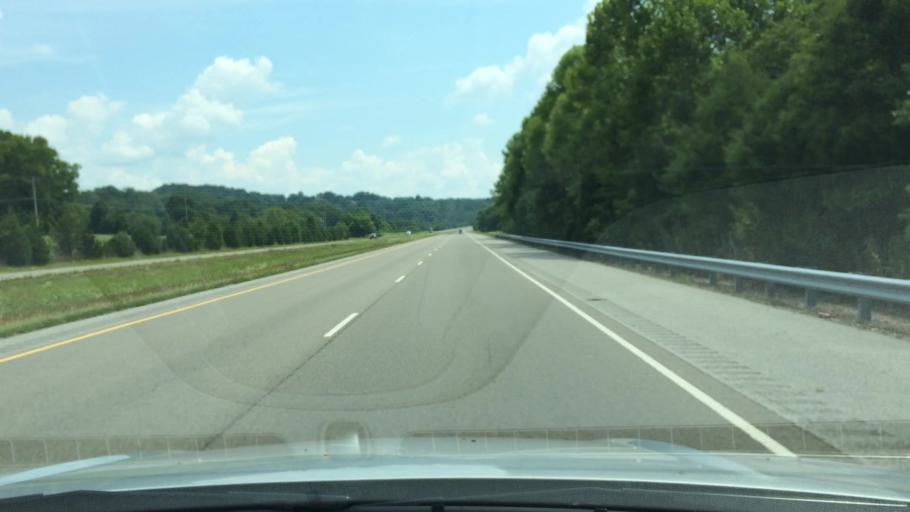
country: US
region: Tennessee
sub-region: Giles County
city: Pulaski
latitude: 35.1714
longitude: -87.0089
